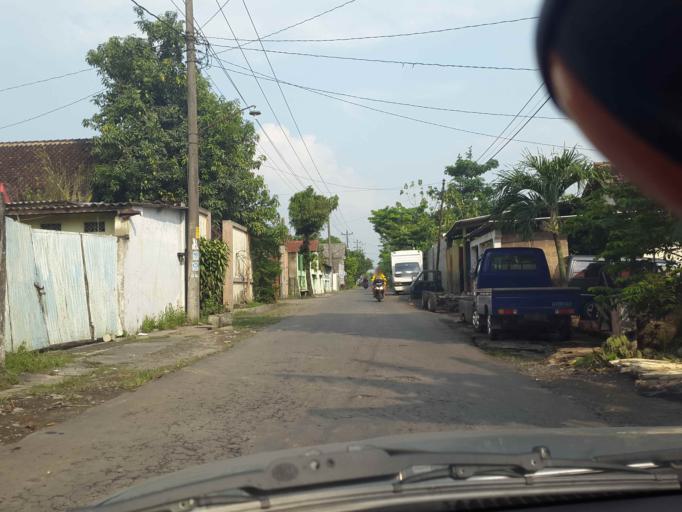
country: ID
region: Central Java
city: Jaten
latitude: -7.5626
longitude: 110.8666
